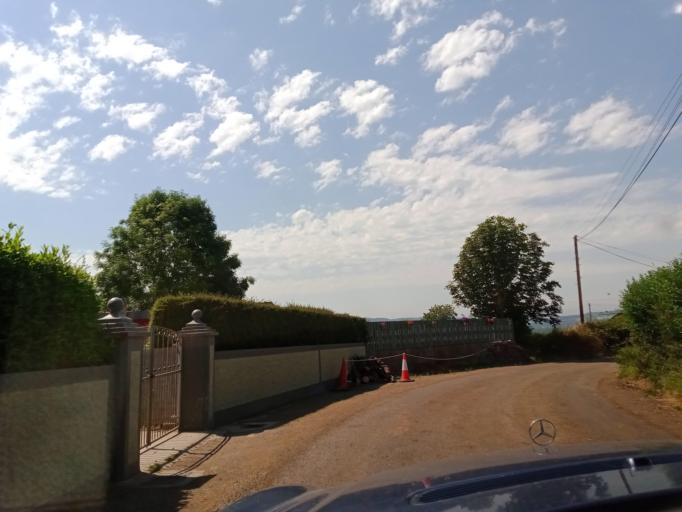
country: IE
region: Leinster
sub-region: Kilkenny
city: Mooncoin
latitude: 52.2686
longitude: -7.2347
